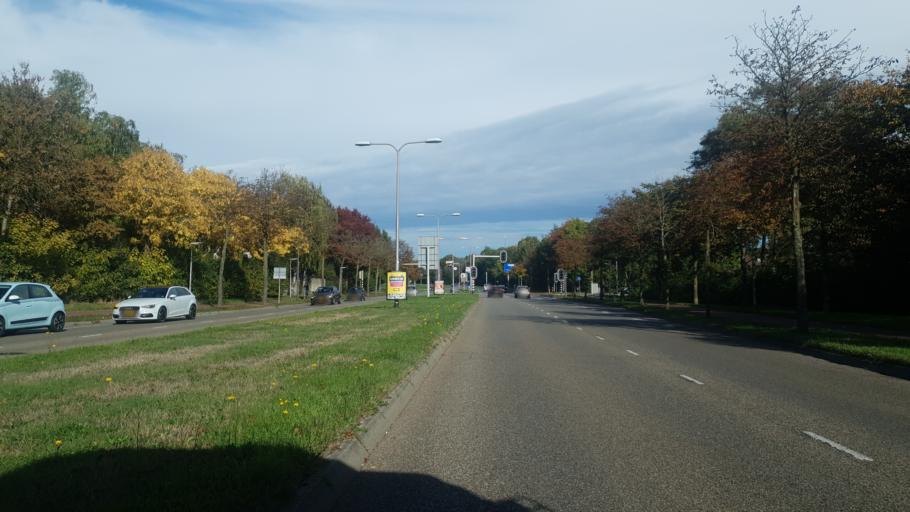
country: NL
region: Gelderland
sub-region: Gemeente Nijmegen
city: Lindenholt
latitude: 51.8346
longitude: 5.7987
